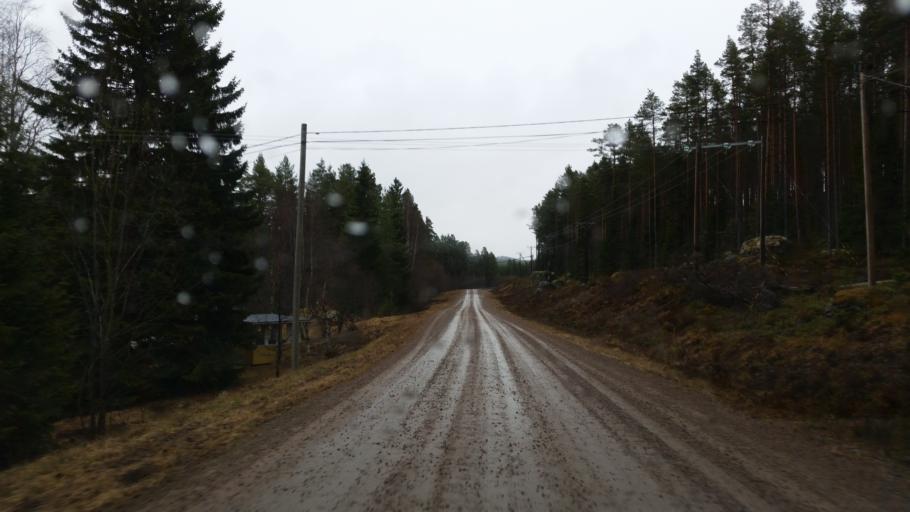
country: SE
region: Vaesternorrland
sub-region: Ange Kommun
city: Ange
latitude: 62.1677
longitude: 15.6514
